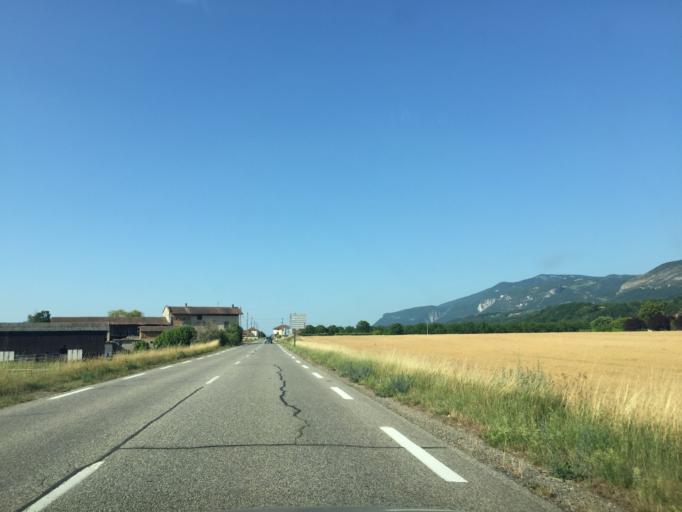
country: FR
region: Rhone-Alpes
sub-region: Departement de l'Isere
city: Saint-Just-de-Claix
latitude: 45.0862
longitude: 5.2950
